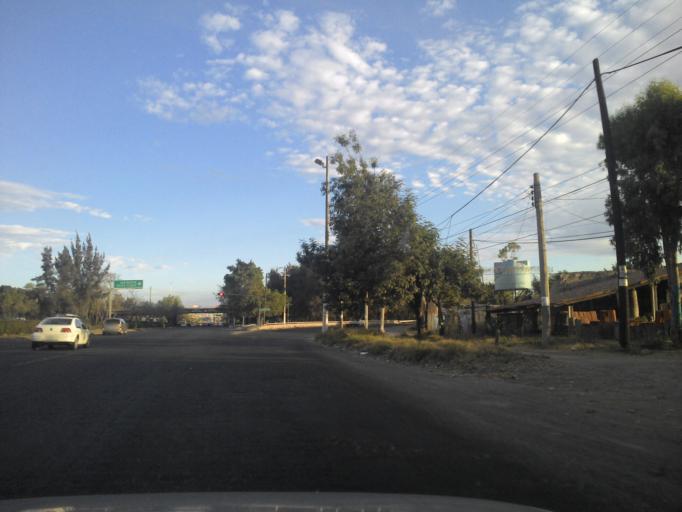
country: MX
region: Jalisco
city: Las Pintas de Arriba
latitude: 20.5929
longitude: -103.3229
